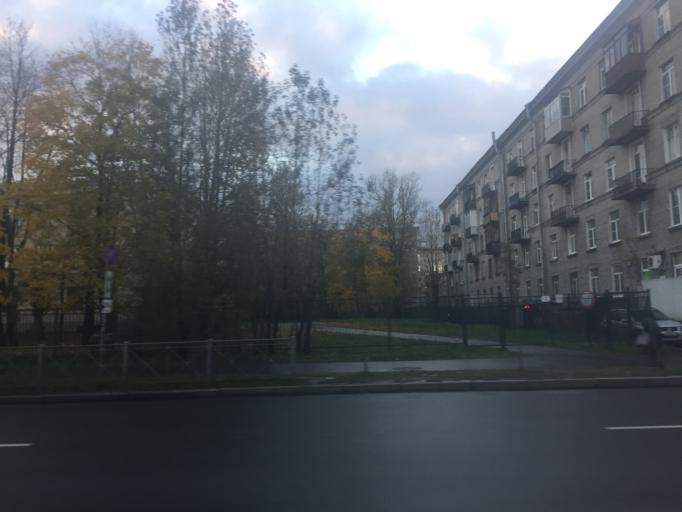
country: RU
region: St.-Petersburg
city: Obukhovo
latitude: 59.8795
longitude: 30.4394
